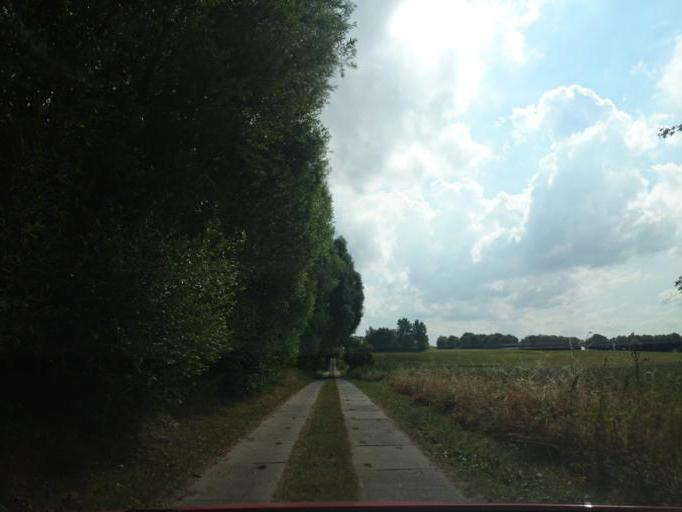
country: DE
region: Mecklenburg-Vorpommern
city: Barth
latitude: 54.3616
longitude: 12.7513
